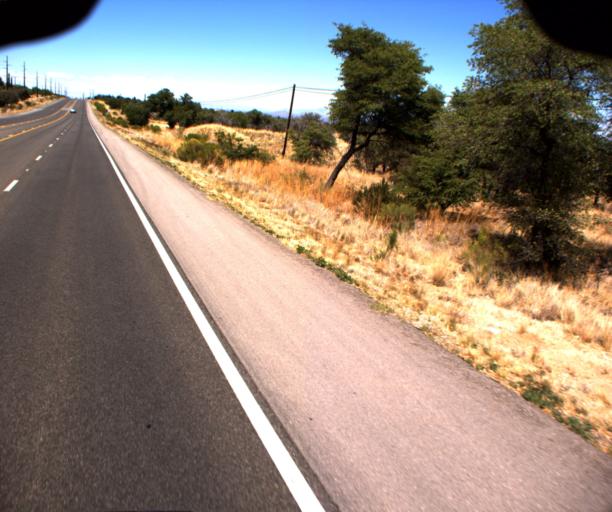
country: US
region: Arizona
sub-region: Cochise County
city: Sierra Vista Southeast
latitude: 31.4157
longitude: -110.2407
